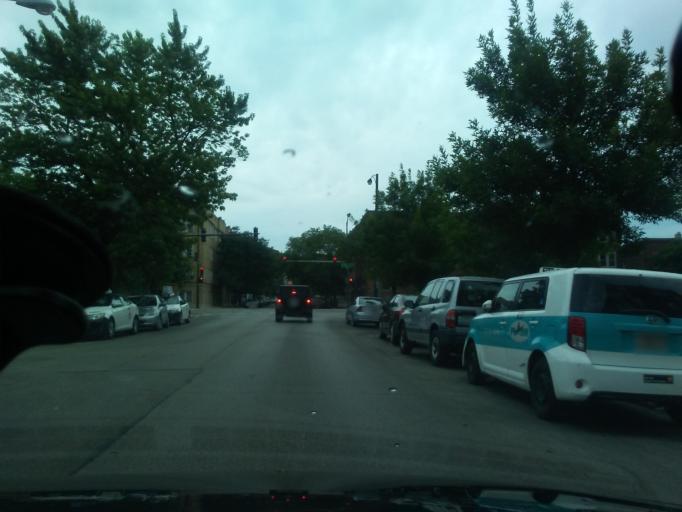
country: US
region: Illinois
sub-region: Cook County
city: Lincolnwood
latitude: 41.9734
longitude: -87.6703
